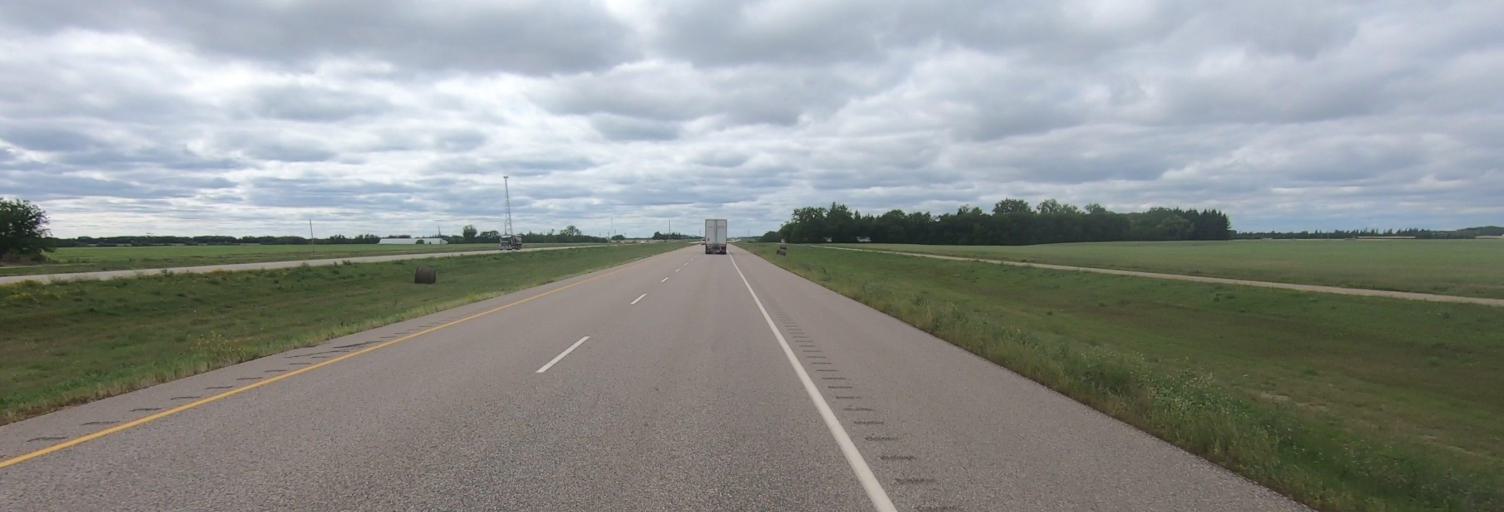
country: CA
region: Manitoba
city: Carberry
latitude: 49.9015
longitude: -99.3281
